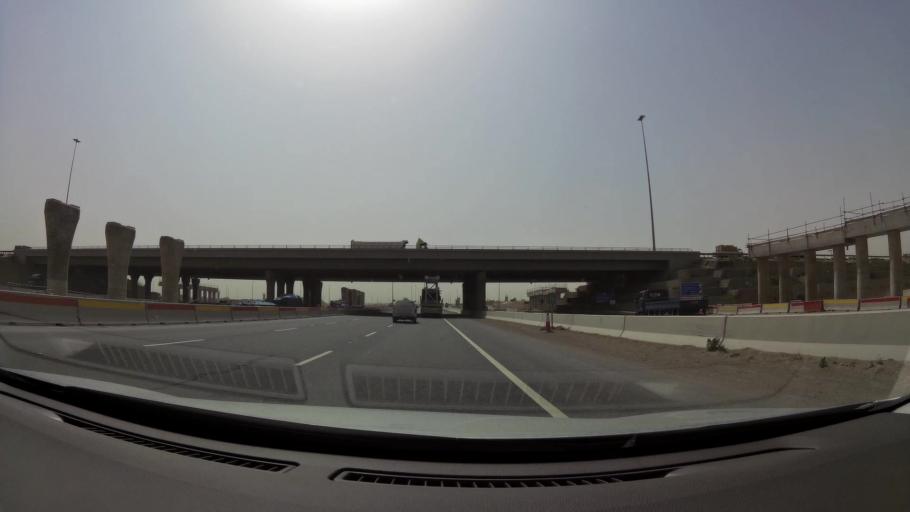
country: QA
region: Baladiyat ar Rayyan
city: Ar Rayyan
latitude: 25.1731
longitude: 51.3278
